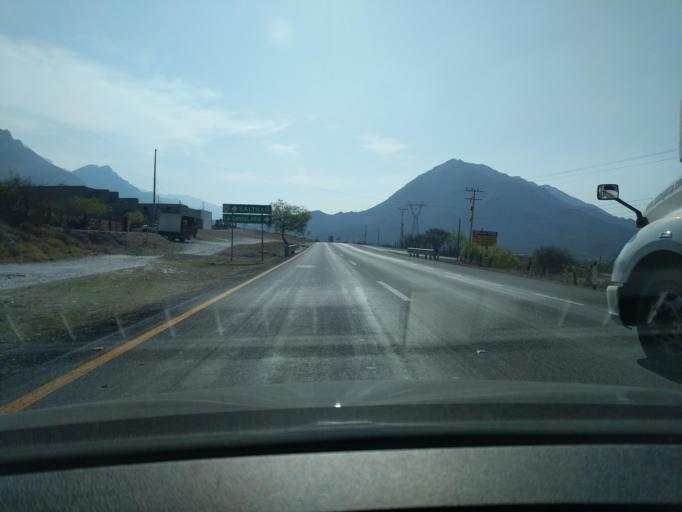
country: MX
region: Nuevo Leon
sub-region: Garcia
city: Las Torres de Guadalupe
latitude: 25.6698
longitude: -100.7003
